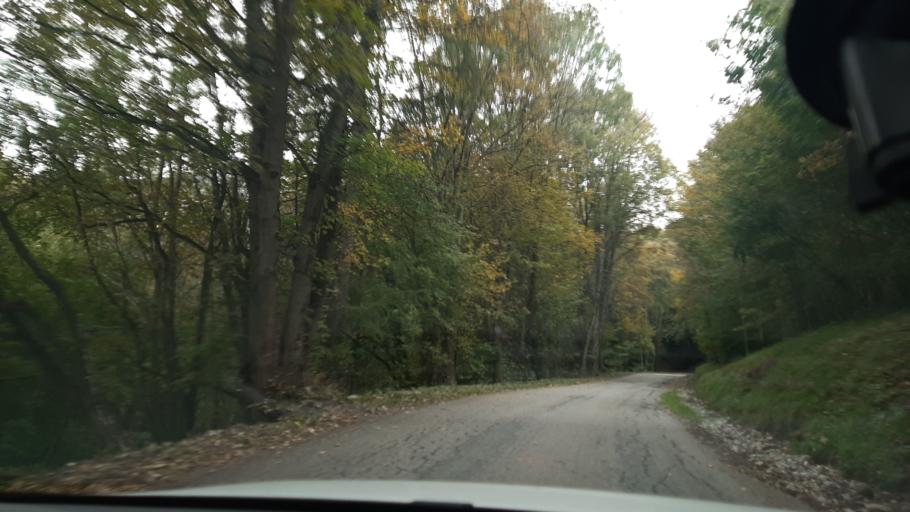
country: FR
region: Rhone-Alpes
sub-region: Departement de la Savoie
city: Villargondran
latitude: 45.2552
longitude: 6.3594
